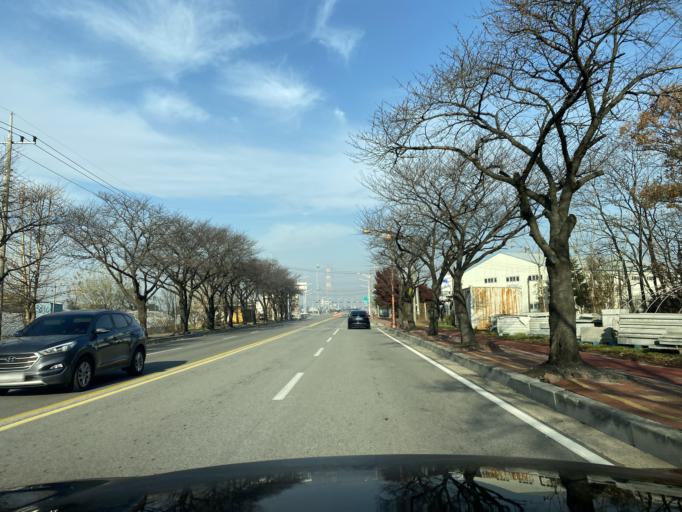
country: KR
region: Chungcheongnam-do
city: Yesan
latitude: 36.7372
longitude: 126.8610
